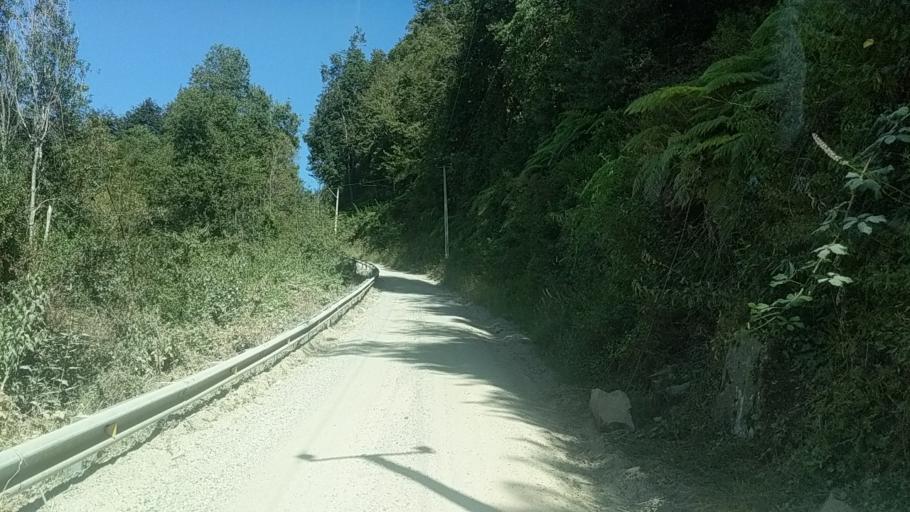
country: CL
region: Araucania
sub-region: Provincia de Cautin
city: Pucon
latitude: -39.0634
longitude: -71.7263
